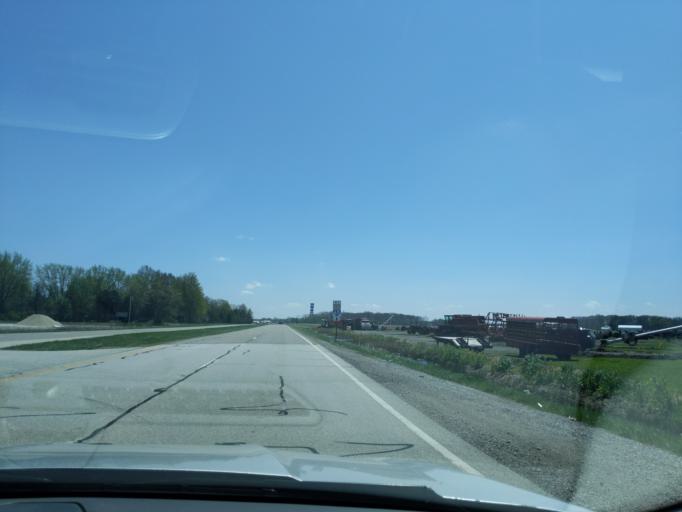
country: US
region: Indiana
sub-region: Boone County
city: Thorntown
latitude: 40.1262
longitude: -86.5609
